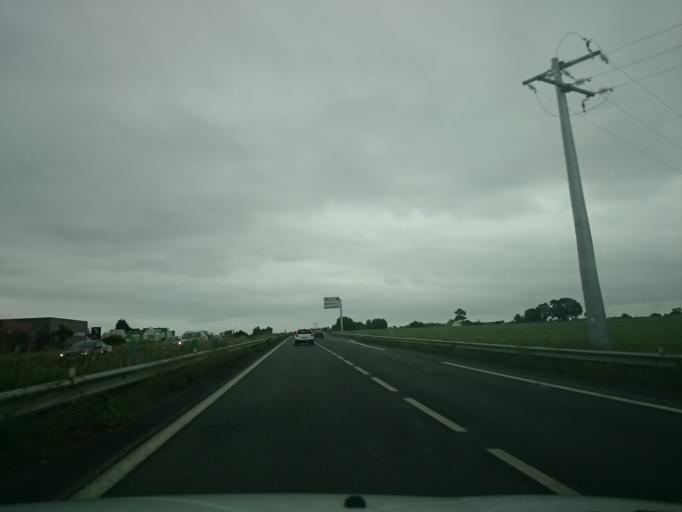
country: FR
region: Brittany
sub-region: Departement des Cotes-d'Armor
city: Lamballe
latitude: 48.4697
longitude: -2.5527
